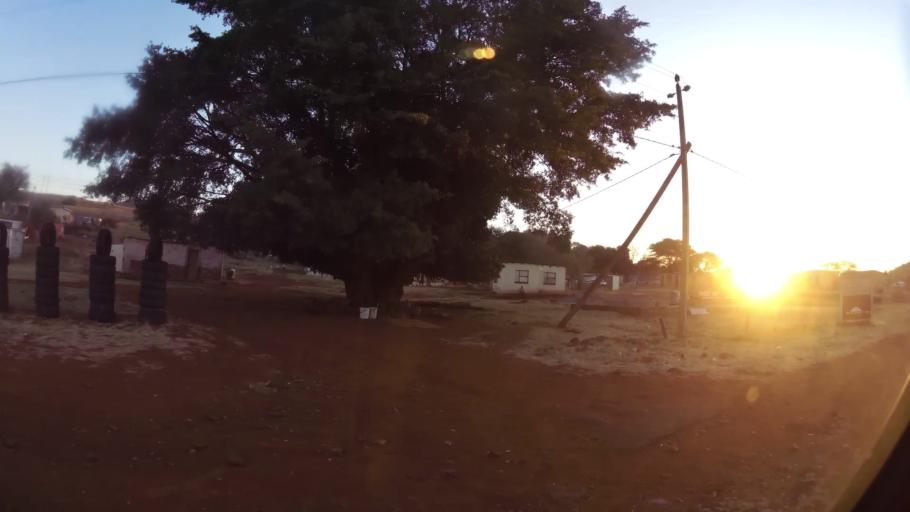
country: ZA
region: North-West
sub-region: Bojanala Platinum District Municipality
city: Rustenburg
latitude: -25.6286
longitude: 27.1991
